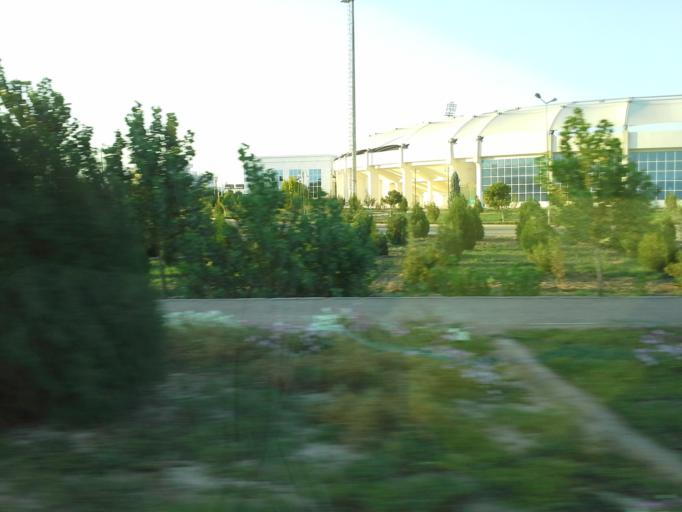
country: TM
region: Dasoguz
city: Dasoguz
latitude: 41.8244
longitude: 59.9341
